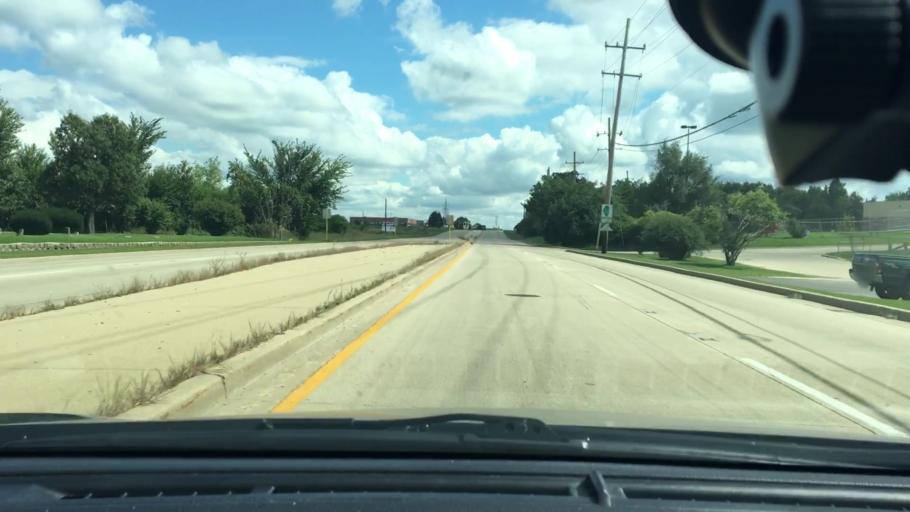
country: US
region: Illinois
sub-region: Kane County
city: East Dundee
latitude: 42.0927
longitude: -88.2563
